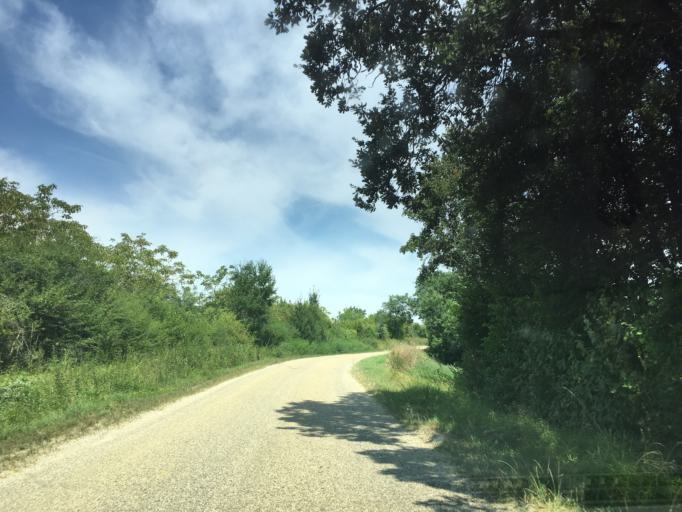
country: FR
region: Midi-Pyrenees
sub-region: Departement du Gers
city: Jegun
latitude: 43.7942
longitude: 0.4907
